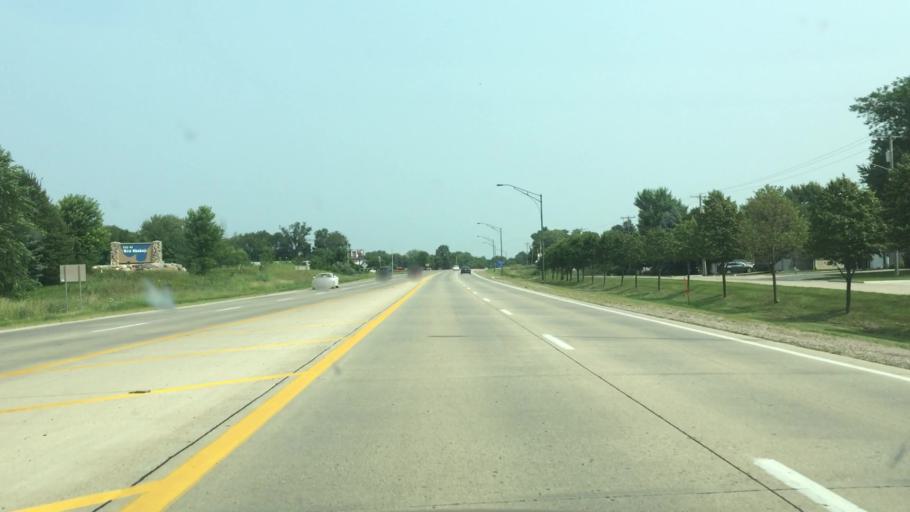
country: US
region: Iowa
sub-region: Dickinson County
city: Arnolds Park
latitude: 43.3545
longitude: -95.1421
